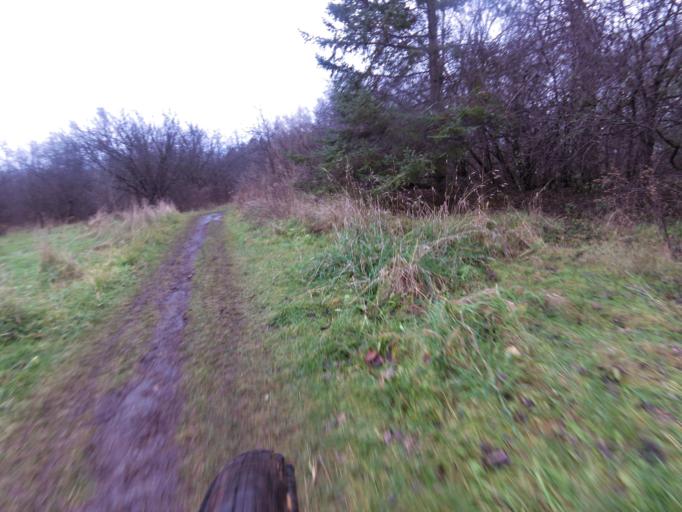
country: CA
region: Ontario
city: Bells Corners
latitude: 45.3141
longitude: -75.8171
